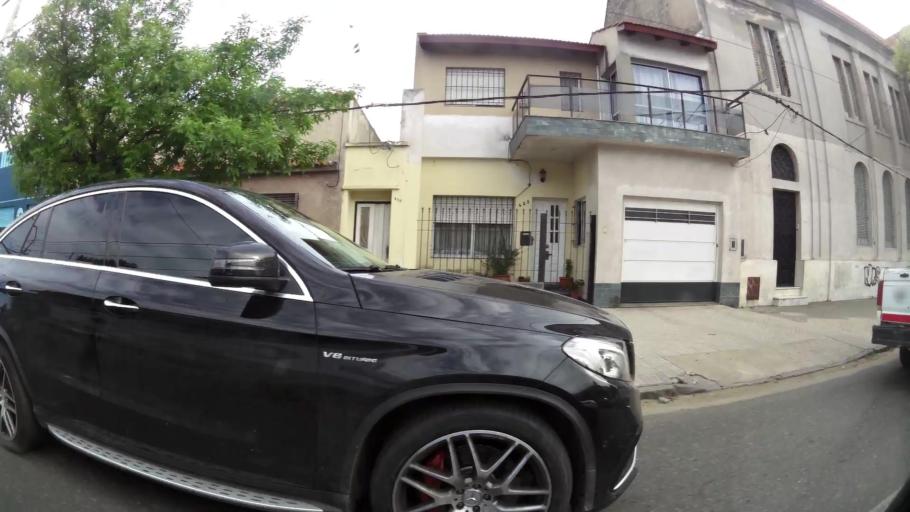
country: AR
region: Santa Fe
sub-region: Departamento de Rosario
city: Rosario
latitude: -32.9248
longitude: -60.6698
